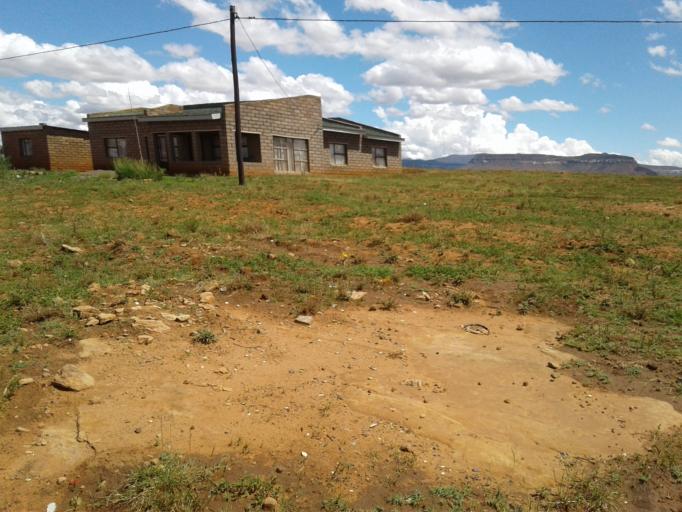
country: LS
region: Quthing
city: Quthing
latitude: -30.3857
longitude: 27.5566
